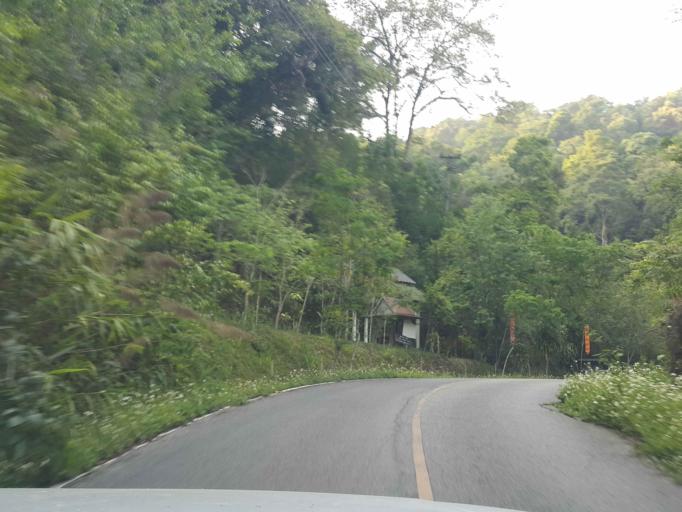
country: TH
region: Chiang Mai
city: Mae On
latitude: 18.9333
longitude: 99.3475
